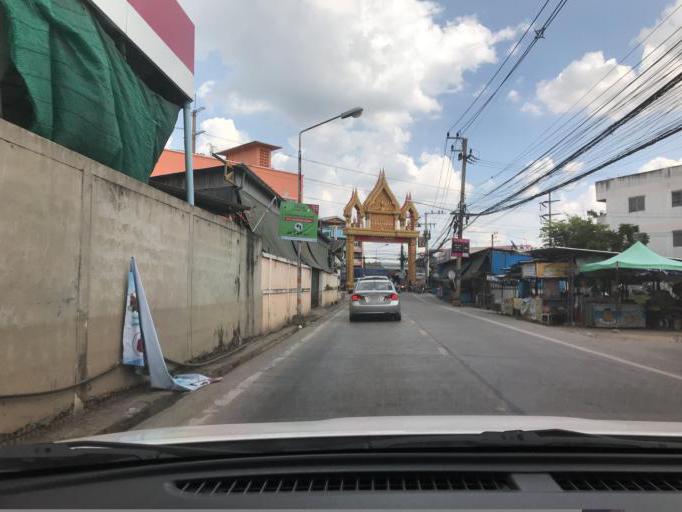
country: TH
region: Phra Nakhon Si Ayutthaya
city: Ban Bang Kadi Pathum Thani
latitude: 14.0004
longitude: 100.5549
